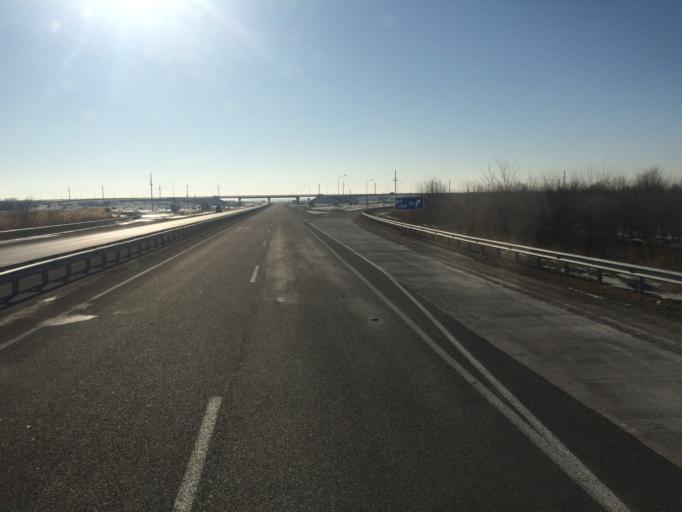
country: KG
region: Chuy
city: Sokuluk
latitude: 43.2793
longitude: 74.2338
